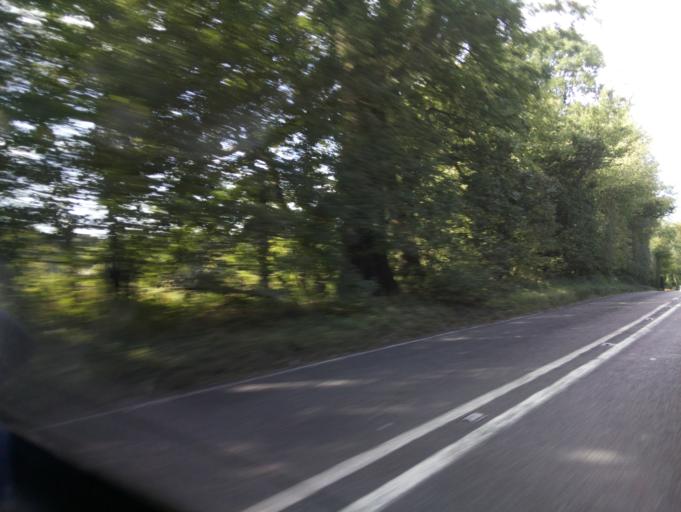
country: GB
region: England
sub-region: Hampshire
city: Basingstoke
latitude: 51.2206
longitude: -1.0620
